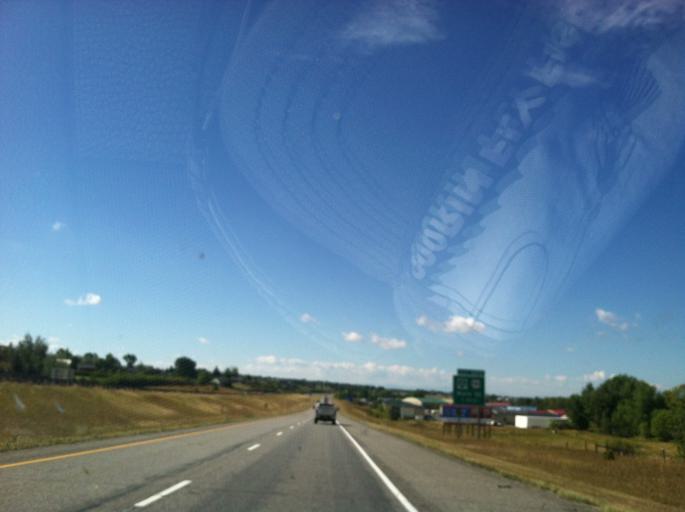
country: US
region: Montana
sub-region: Gallatin County
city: Bozeman
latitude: 45.6693
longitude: -110.9918
